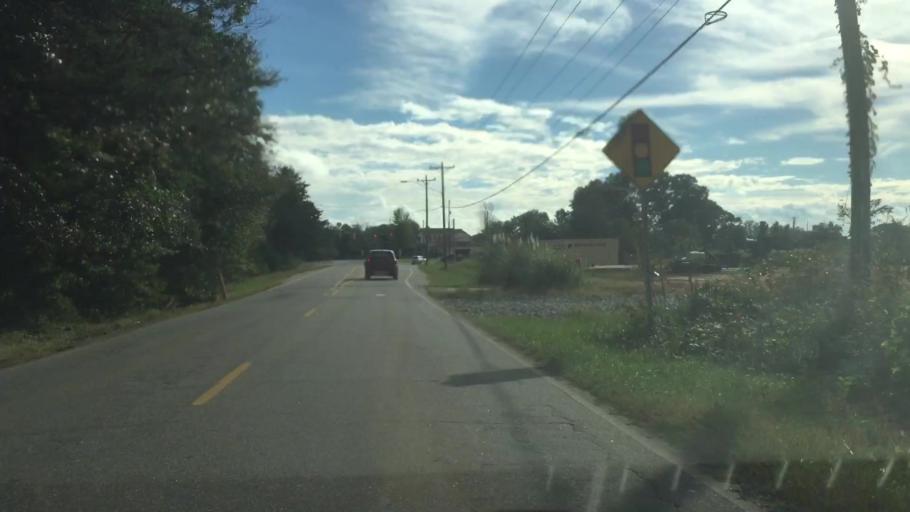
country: US
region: North Carolina
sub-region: Iredell County
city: Mooresville
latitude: 35.5813
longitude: -80.8524
